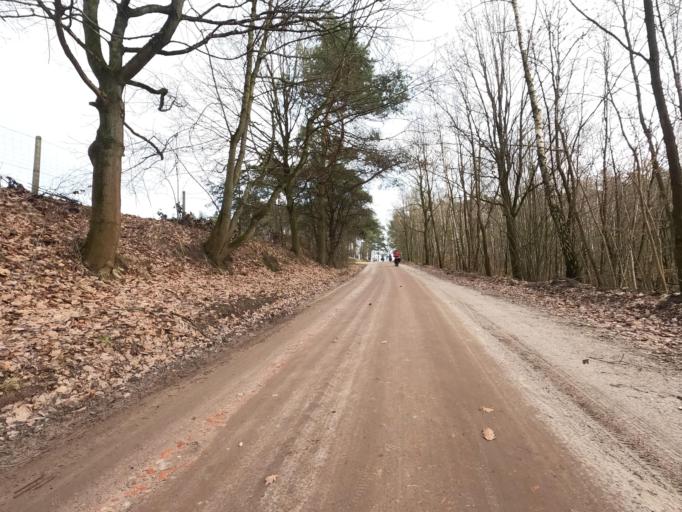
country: PL
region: Greater Poland Voivodeship
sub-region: Powiat pilski
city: Miasteczko Krajenskie
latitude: 53.1017
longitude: 17.0480
